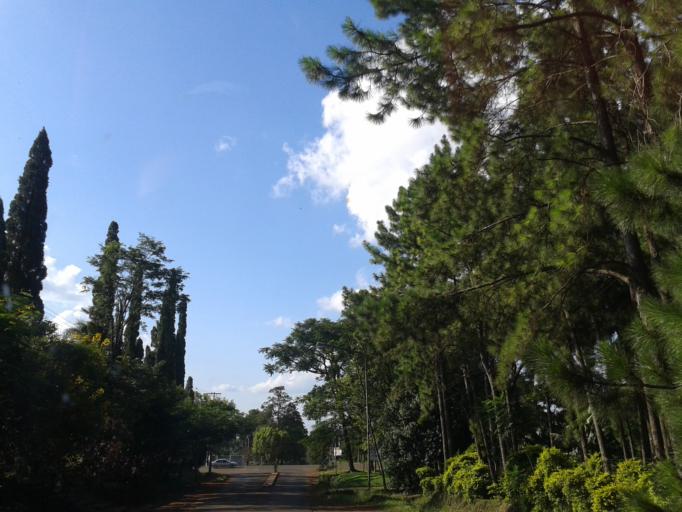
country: AR
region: Misiones
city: Guarani
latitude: -27.4940
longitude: -55.1600
